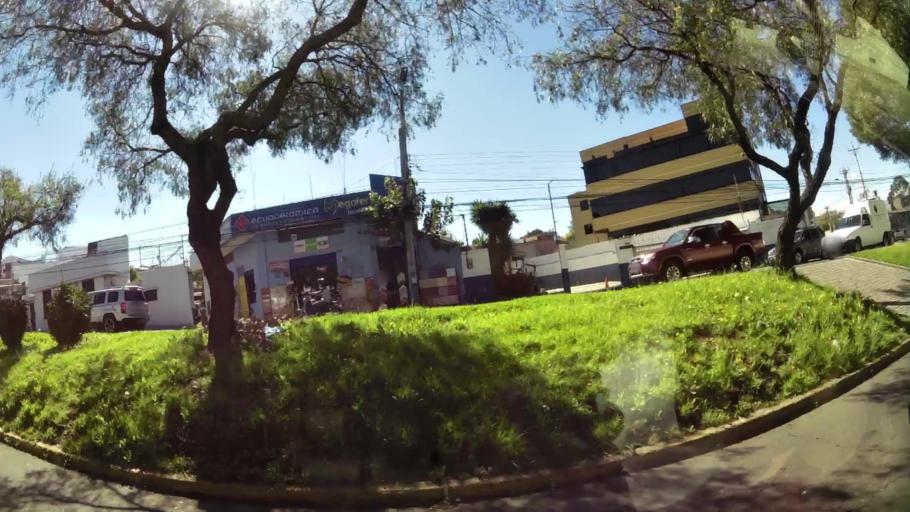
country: EC
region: Pichincha
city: Quito
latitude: -0.1416
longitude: -78.4701
